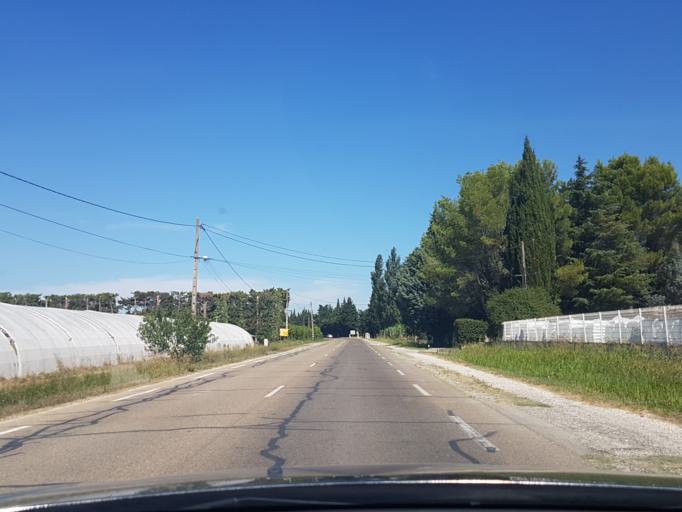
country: FR
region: Provence-Alpes-Cote d'Azur
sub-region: Departement des Bouches-du-Rhone
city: Eyragues
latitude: 43.8549
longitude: 4.8407
